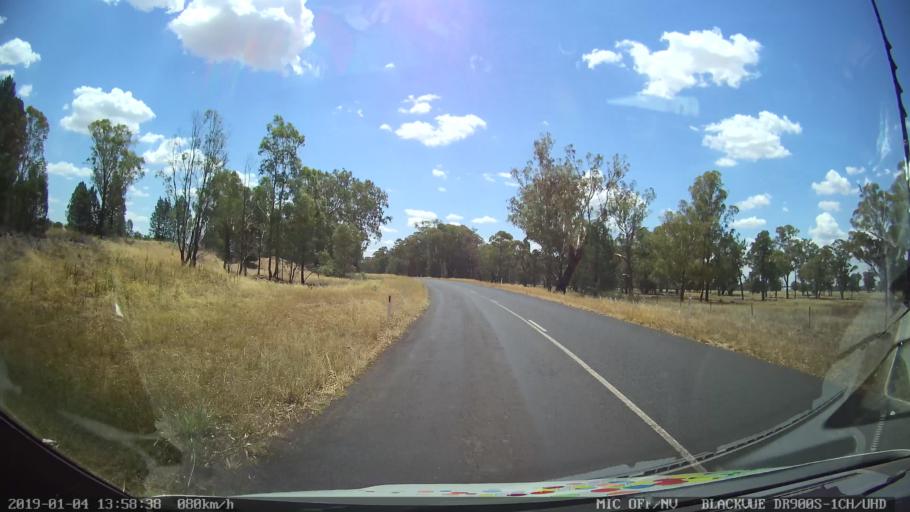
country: AU
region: New South Wales
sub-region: Dubbo Municipality
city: Dubbo
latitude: -32.3262
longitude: 148.5941
